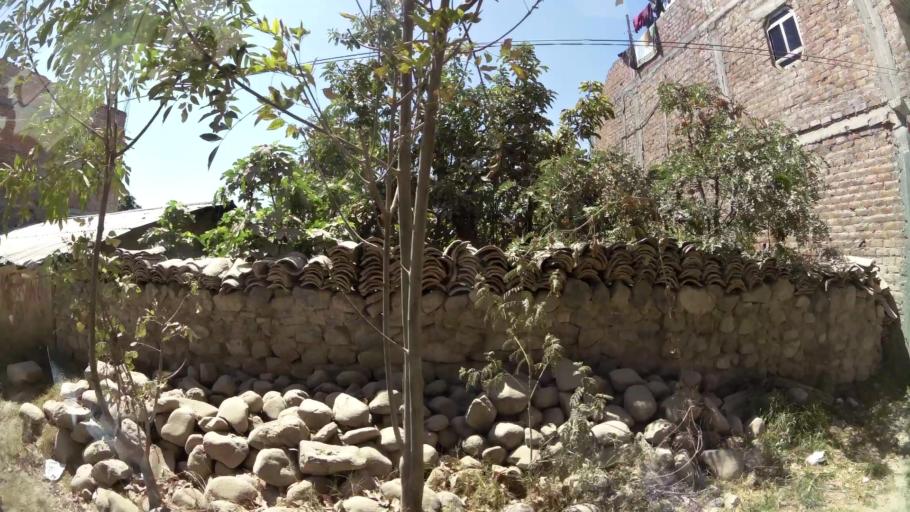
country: PE
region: Ayacucho
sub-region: Provincia de Huamanga
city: Carmen Alto
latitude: -13.1731
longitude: -74.2291
